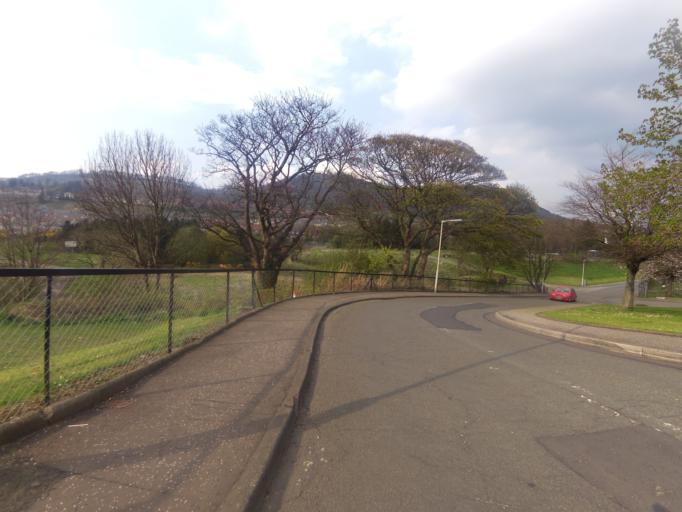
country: GB
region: Scotland
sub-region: Fife
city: Burntisland
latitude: 56.0596
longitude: -3.2432
